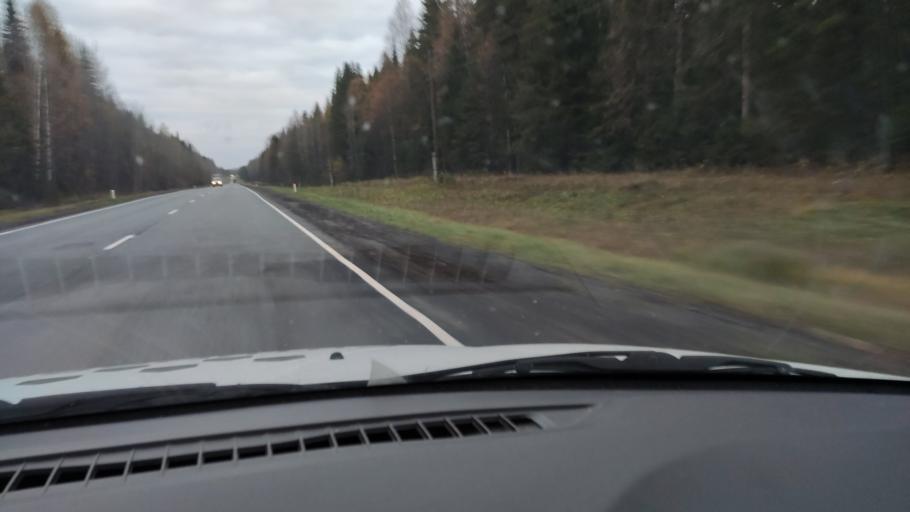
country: RU
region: Kirov
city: Belorechensk
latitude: 58.8044
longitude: 52.4363
